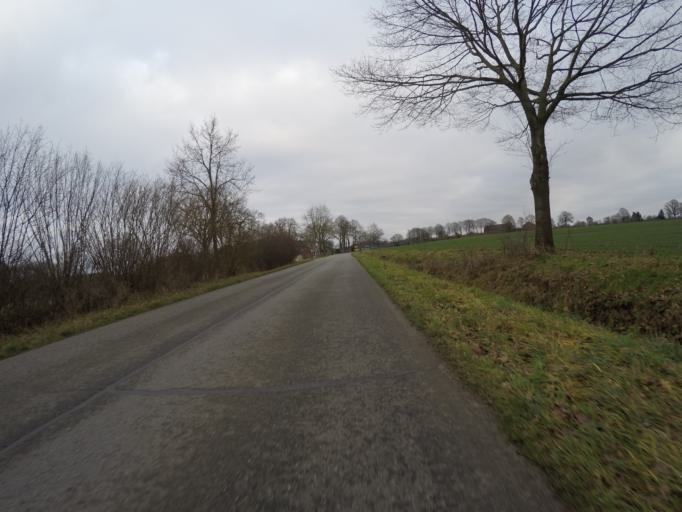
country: DE
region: Schleswig-Holstein
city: Langeln
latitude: 53.7931
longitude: 9.8451
